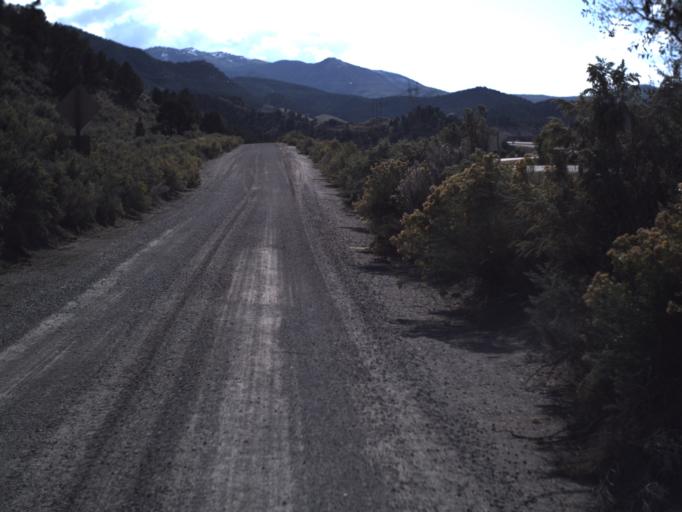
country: US
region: Utah
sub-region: Sevier County
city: Monroe
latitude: 38.5695
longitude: -112.3503
